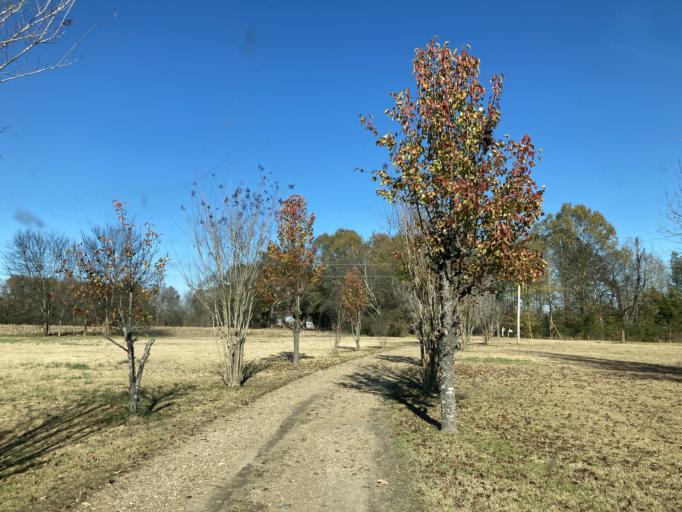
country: US
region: Mississippi
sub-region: Holmes County
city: Pickens
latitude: 32.8572
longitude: -90.0075
